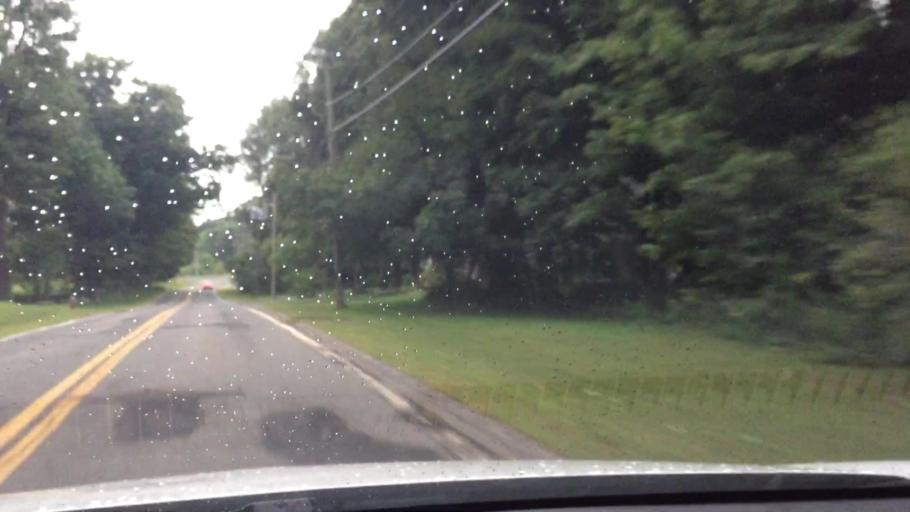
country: US
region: Massachusetts
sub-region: Berkshire County
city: Otis
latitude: 42.2013
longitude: -72.9384
